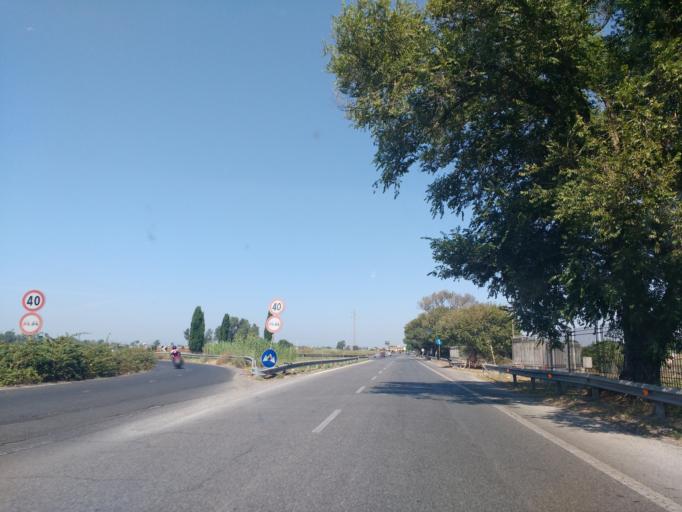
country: IT
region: Latium
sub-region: Citta metropolitana di Roma Capitale
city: Lido di Ostia
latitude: 41.7497
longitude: 12.2852
